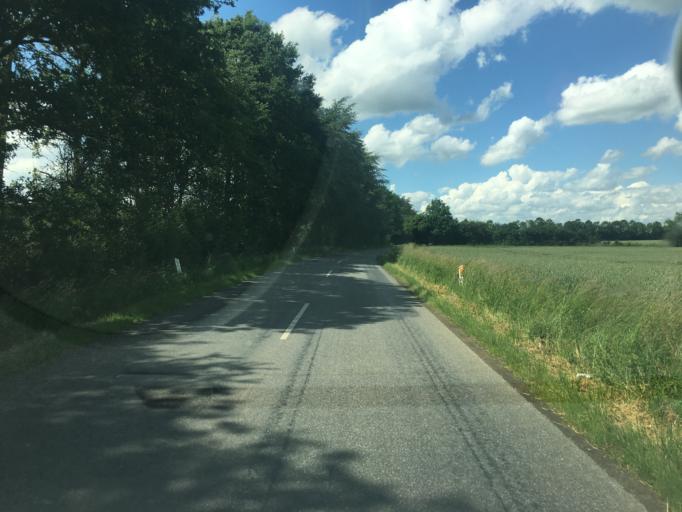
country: DK
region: South Denmark
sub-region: Haderslev Kommune
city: Vojens
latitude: 55.2768
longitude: 9.3271
